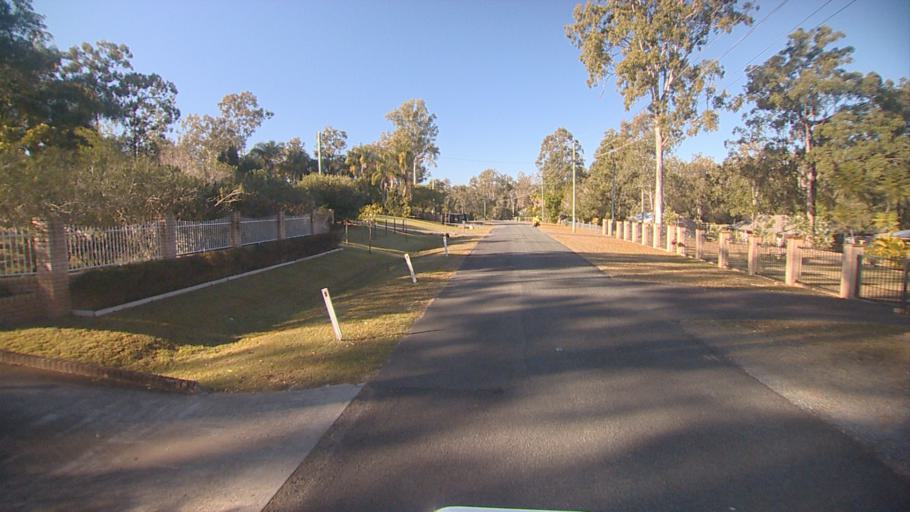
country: AU
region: Queensland
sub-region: Logan
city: North Maclean
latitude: -27.7441
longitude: 153.0161
